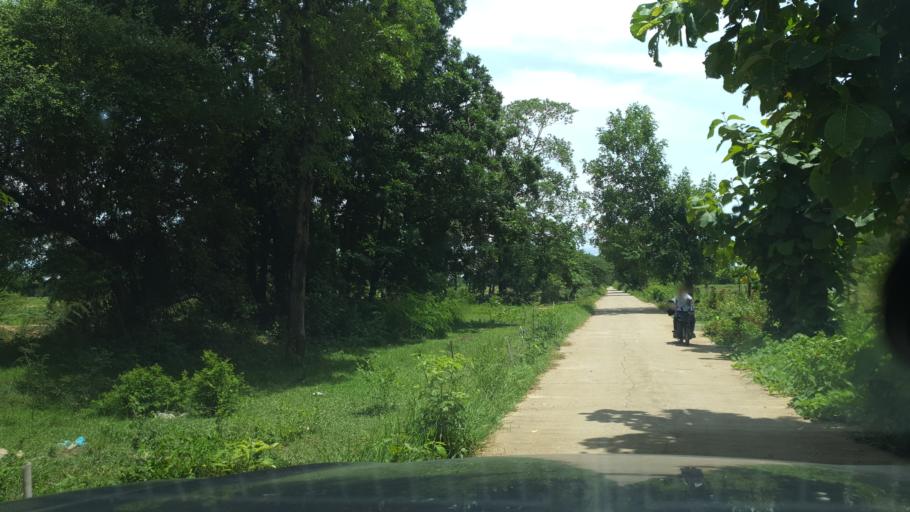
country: TH
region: Sukhothai
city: Ban Na
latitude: 17.0870
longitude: 99.6871
